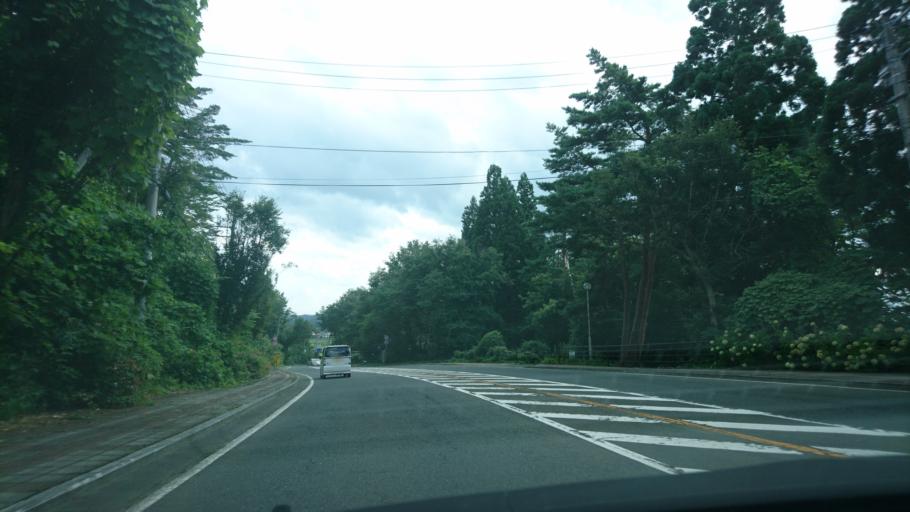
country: JP
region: Iwate
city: Hanamaki
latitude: 39.3972
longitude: 141.1652
